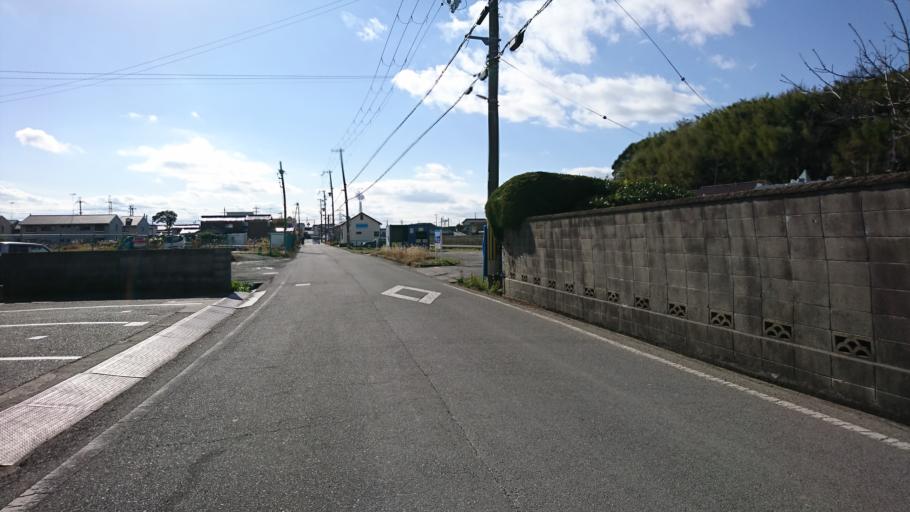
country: JP
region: Hyogo
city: Shirahamacho-usazakiminami
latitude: 34.7775
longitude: 134.7710
